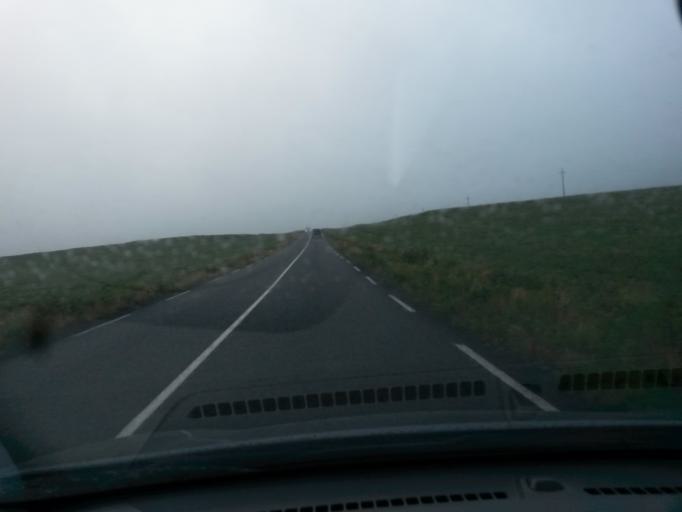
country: IS
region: South
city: Vestmannaeyjar
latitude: 63.5082
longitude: -19.4376
